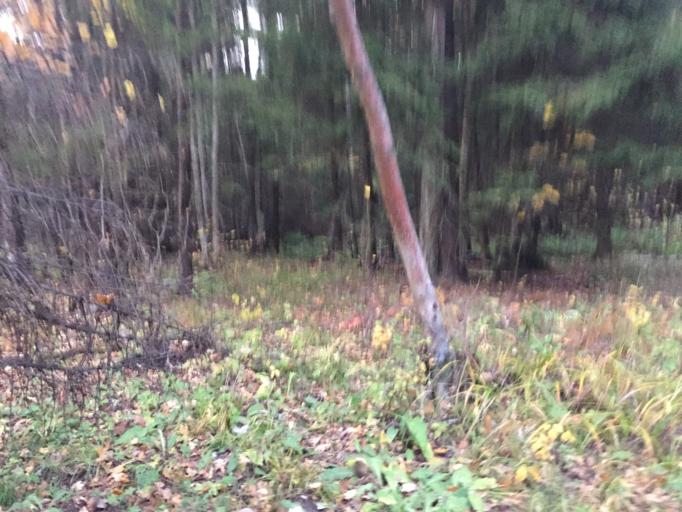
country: RU
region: Moskovskaya
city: Druzhba
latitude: 55.8610
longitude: 37.7810
